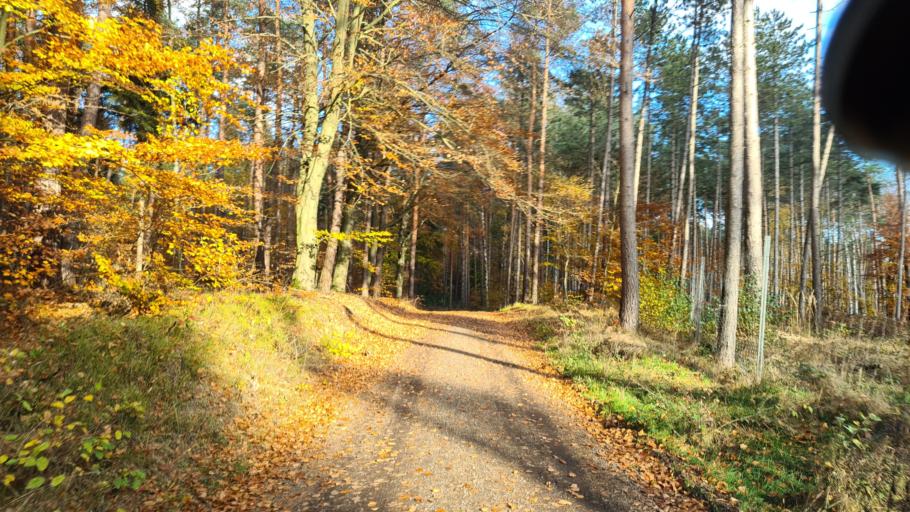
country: DE
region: Saxony
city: Dahlen
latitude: 51.4097
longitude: 12.9923
